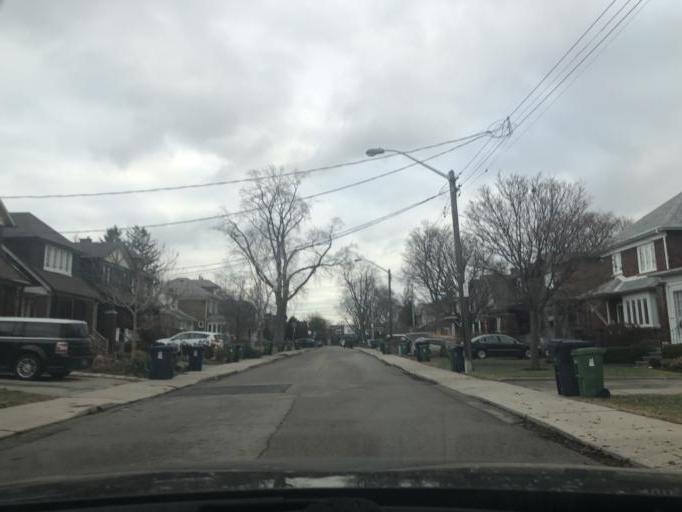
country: CA
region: Ontario
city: Toronto
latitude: 43.6836
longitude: -79.3542
